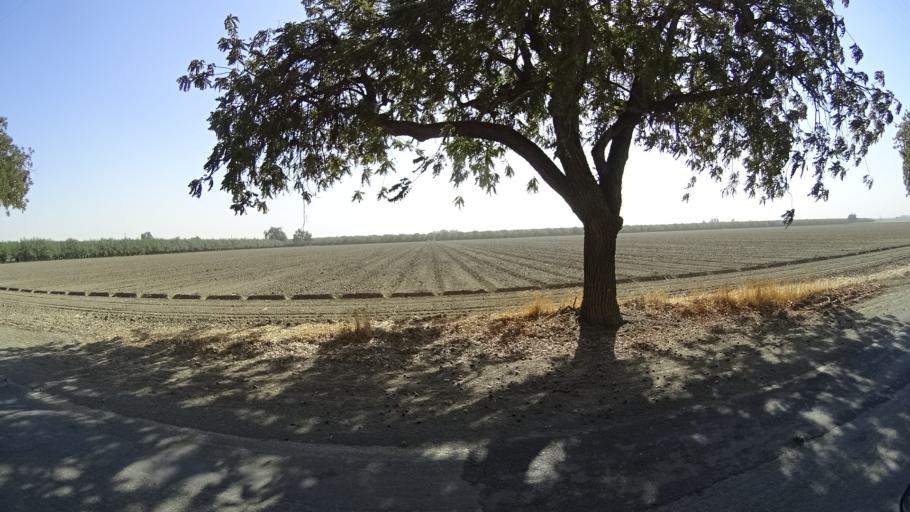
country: US
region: California
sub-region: Yolo County
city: Woodland
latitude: 38.7356
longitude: -121.8266
